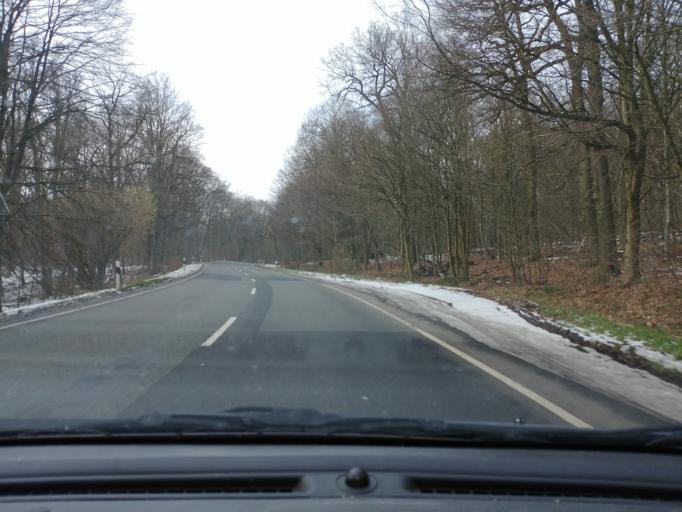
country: DE
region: Lower Saxony
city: Bad Karlshafen
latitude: 51.6896
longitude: 9.4976
